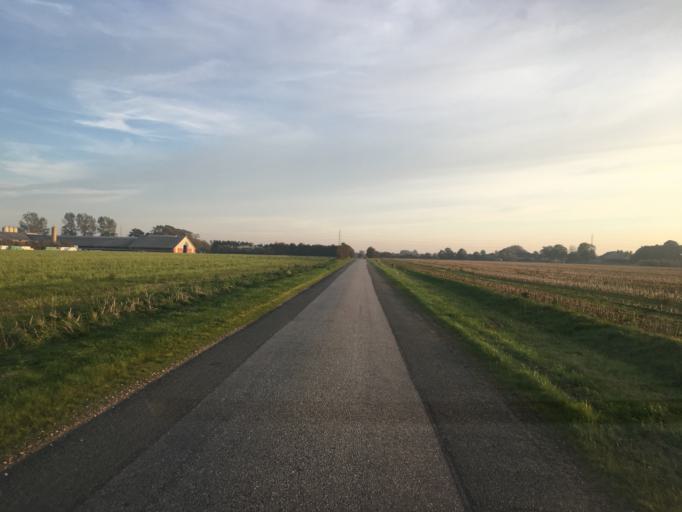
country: DK
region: South Denmark
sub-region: Tonder Kommune
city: Logumkloster
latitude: 55.0446
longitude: 9.0263
